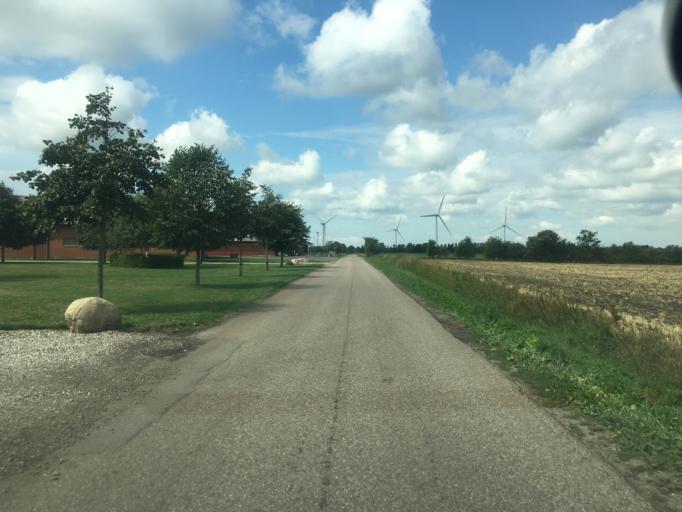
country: DK
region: South Denmark
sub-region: Tonder Kommune
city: Toftlund
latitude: 55.1162
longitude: 9.0364
